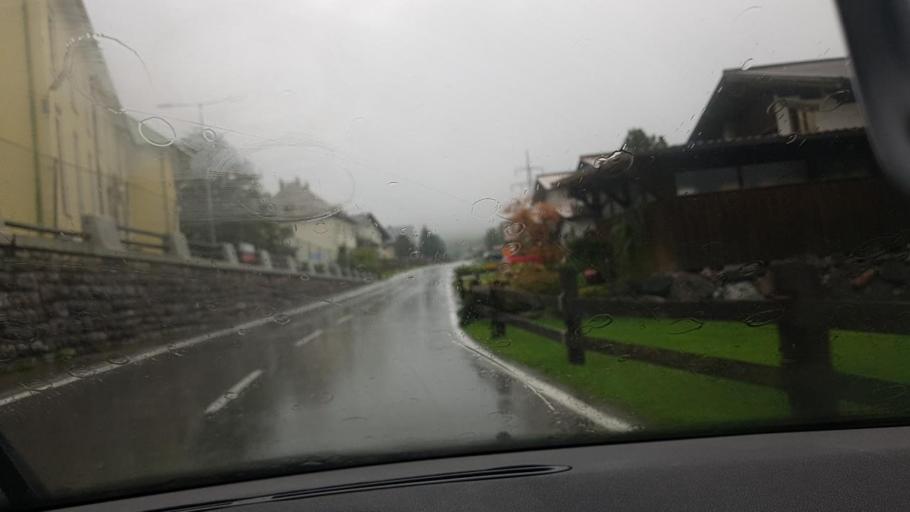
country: AT
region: Vorarlberg
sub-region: Politischer Bezirk Bludenz
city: Klosterle
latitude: 47.1326
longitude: 10.0537
